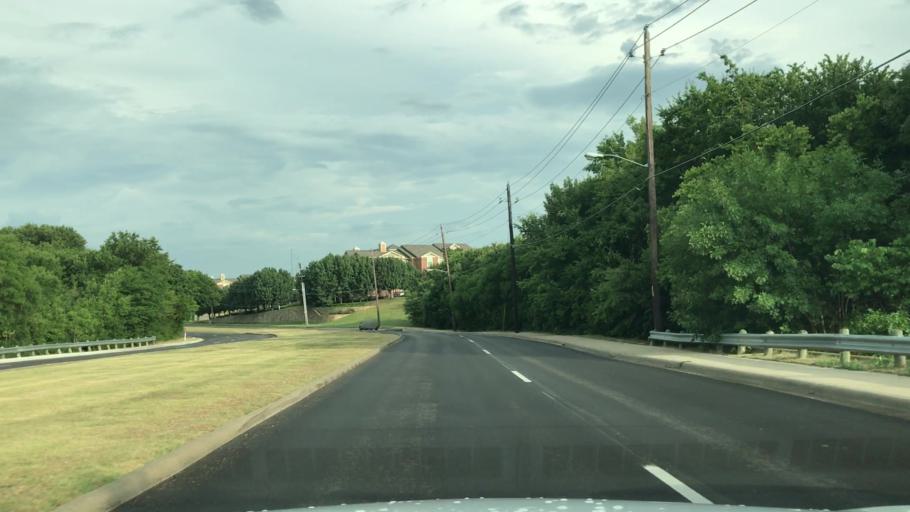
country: US
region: Texas
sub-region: Dallas County
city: Sunnyvale
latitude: 32.8393
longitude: -96.6224
